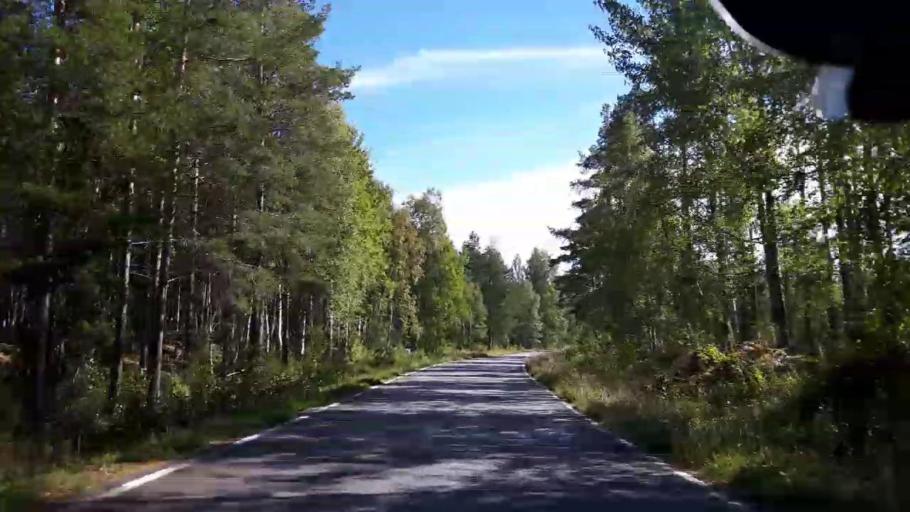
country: SE
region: Jaemtland
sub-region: OEstersunds Kommun
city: Lit
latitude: 63.2268
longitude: 15.2788
